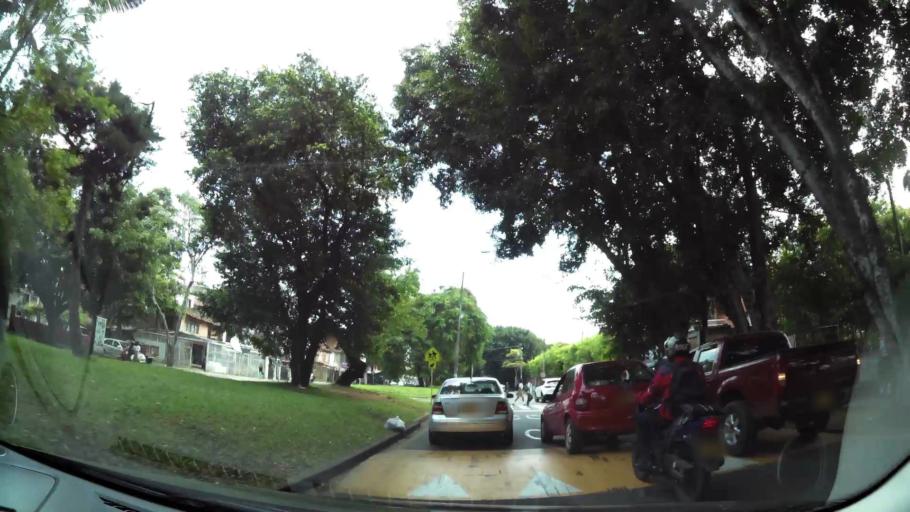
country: CO
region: Valle del Cauca
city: Cali
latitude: 3.4098
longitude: -76.5298
